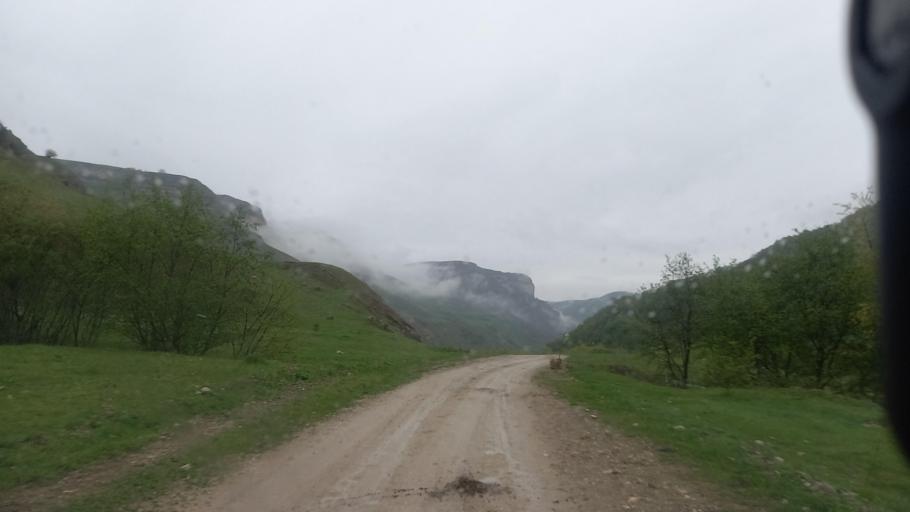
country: RU
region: Kabardino-Balkariya
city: Gundelen
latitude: 43.5974
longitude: 43.0644
